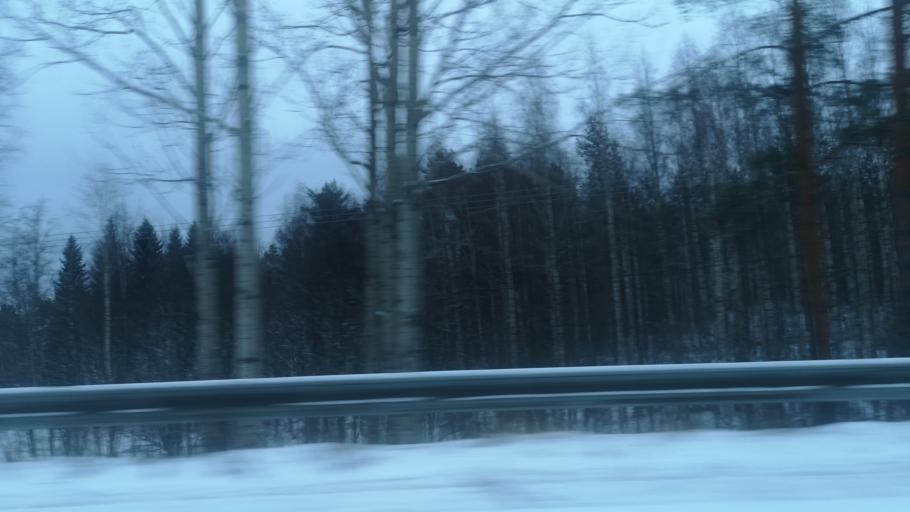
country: FI
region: Southern Savonia
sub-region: Savonlinna
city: Enonkoski
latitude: 62.0969
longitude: 28.6656
